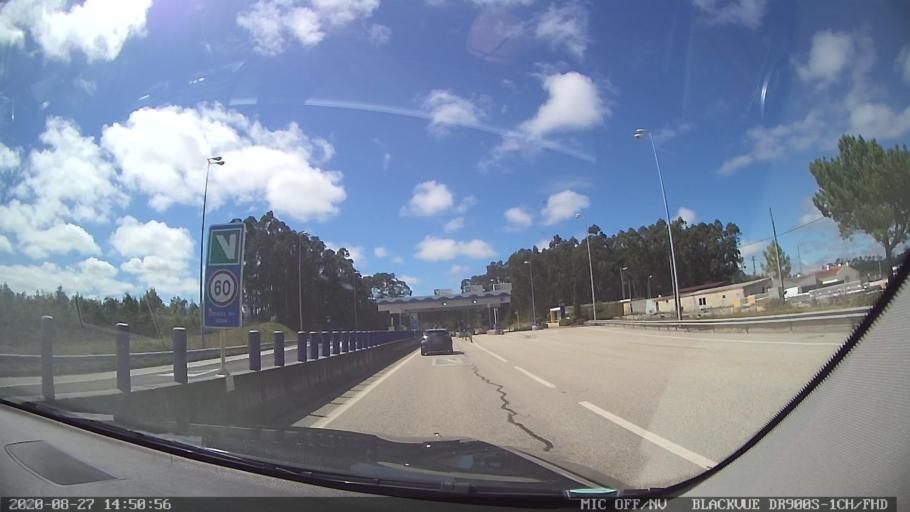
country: PT
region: Leiria
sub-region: Marinha Grande
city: Marinha Grande
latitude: 39.7442
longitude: -8.8747
